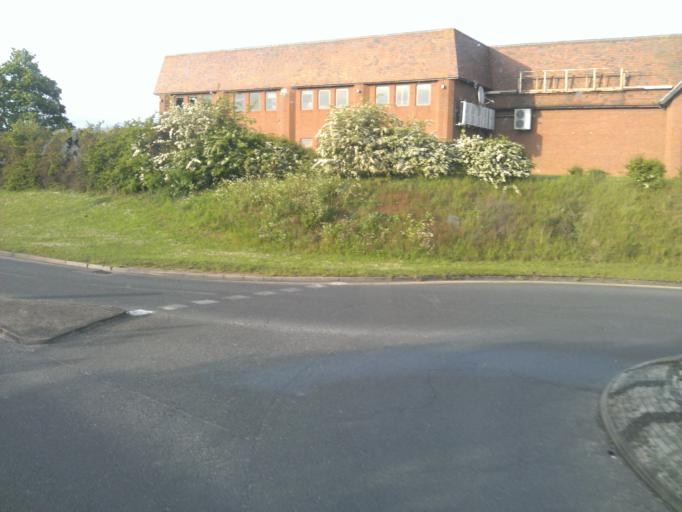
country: GB
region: England
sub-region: Essex
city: Eight Ash Green
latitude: 51.8851
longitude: 0.8348
